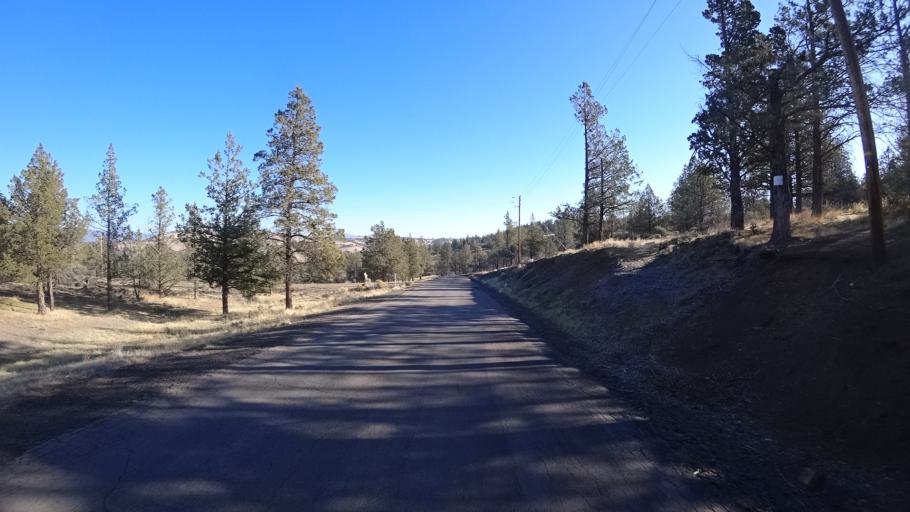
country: US
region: California
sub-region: Siskiyou County
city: Montague
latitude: 41.8819
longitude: -122.4471
